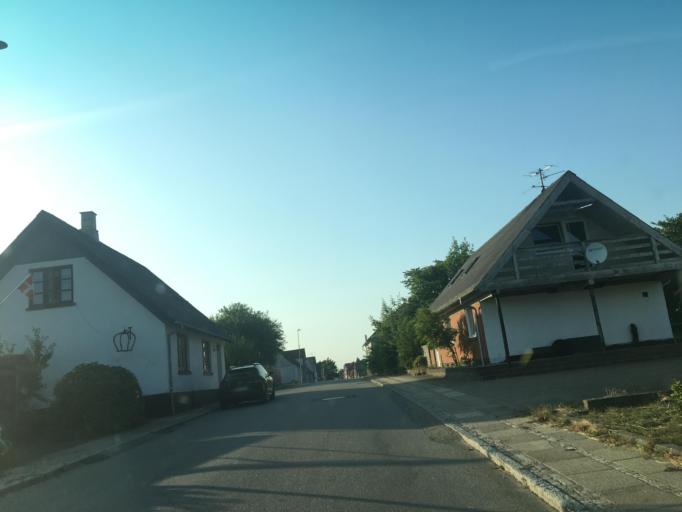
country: DK
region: North Denmark
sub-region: Thisted Kommune
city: Hurup
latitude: 56.8045
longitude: 8.4079
